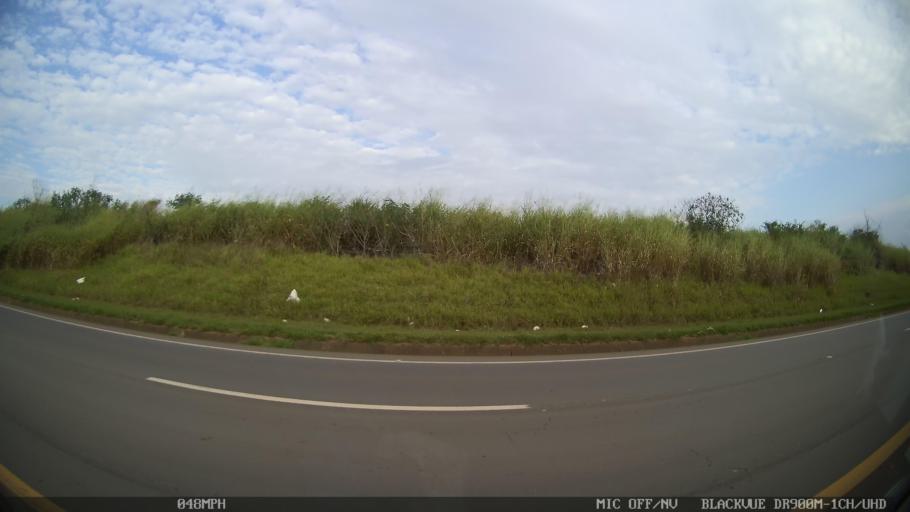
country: BR
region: Sao Paulo
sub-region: Cosmopolis
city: Cosmopolis
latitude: -22.6212
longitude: -47.2525
